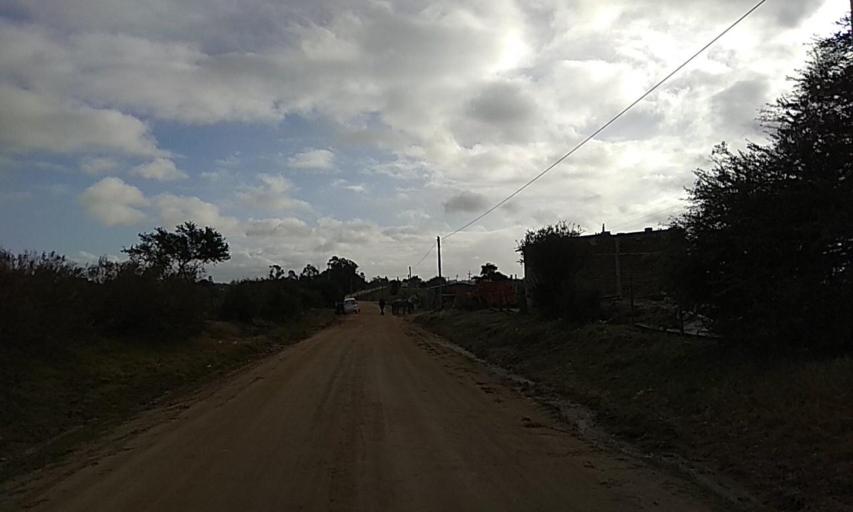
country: UY
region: Florida
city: Florida
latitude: -34.0650
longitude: -56.1935
